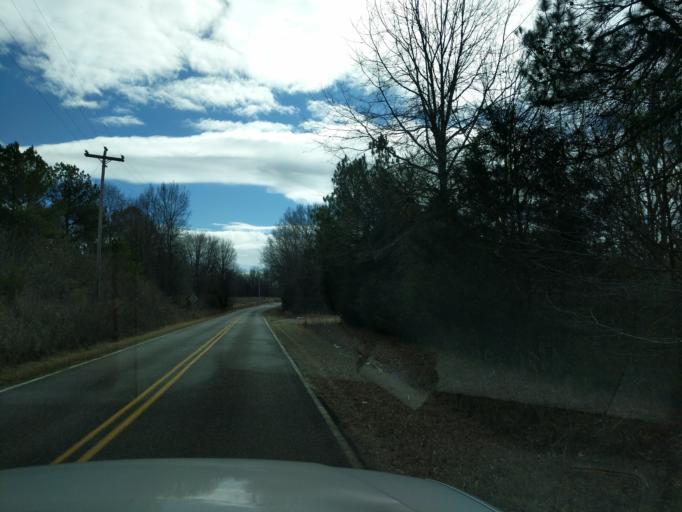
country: US
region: South Carolina
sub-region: Edgefield County
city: Edgefield
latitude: 33.9027
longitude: -82.0006
